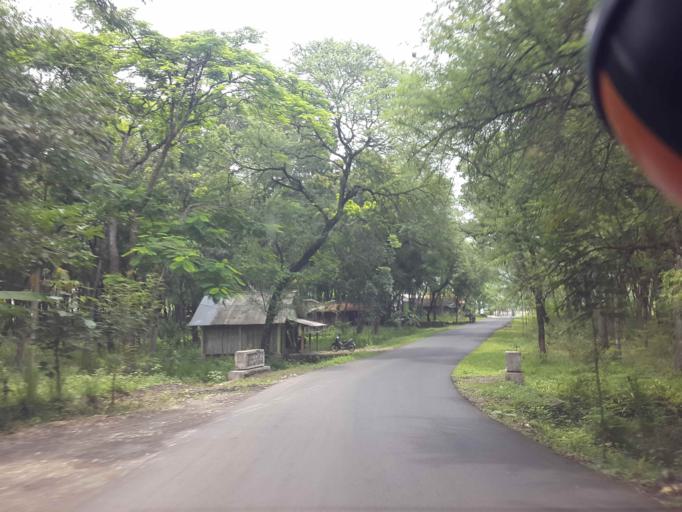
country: ID
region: East Java
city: Ponorogo
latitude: -7.7730
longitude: 111.3512
